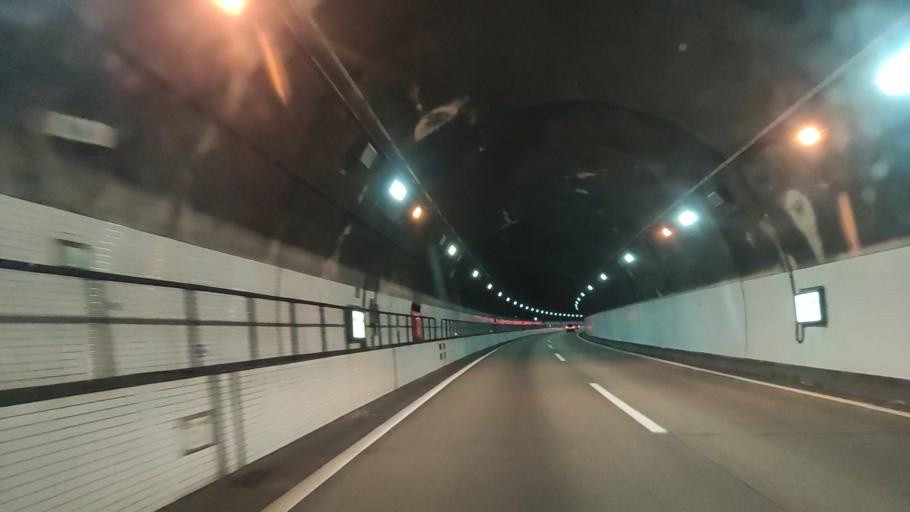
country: JP
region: Ehime
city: Niihama
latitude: 33.9160
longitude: 133.3088
